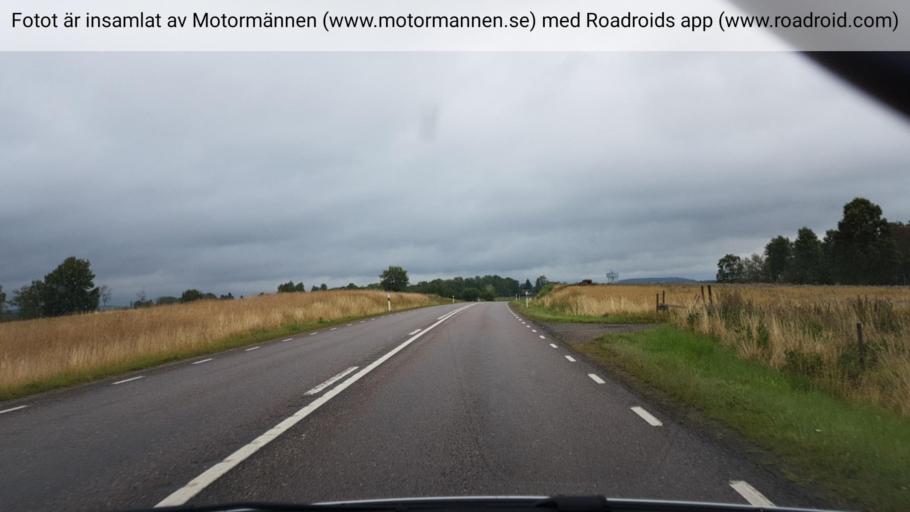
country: SE
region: Vaestra Goetaland
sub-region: Falkopings Kommun
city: Akarp
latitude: 58.2571
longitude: 13.7013
